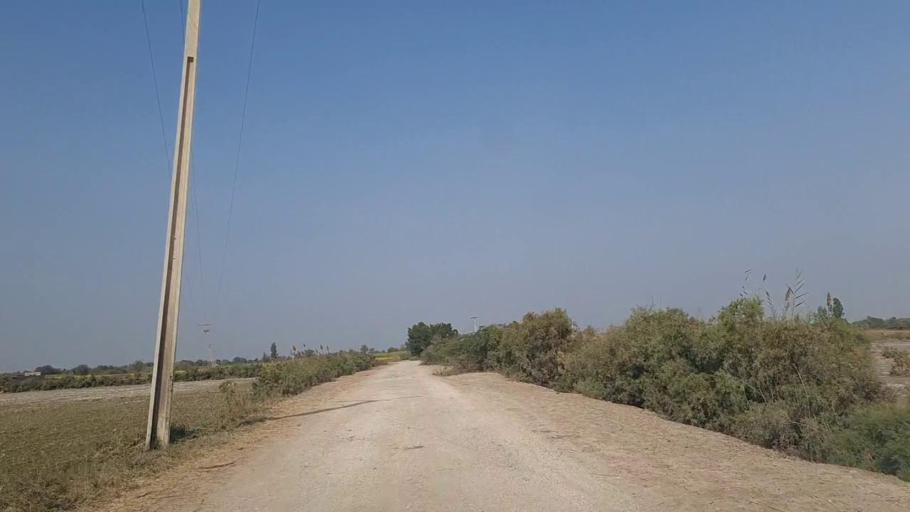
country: PK
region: Sindh
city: Daur
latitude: 26.4871
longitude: 68.4514
